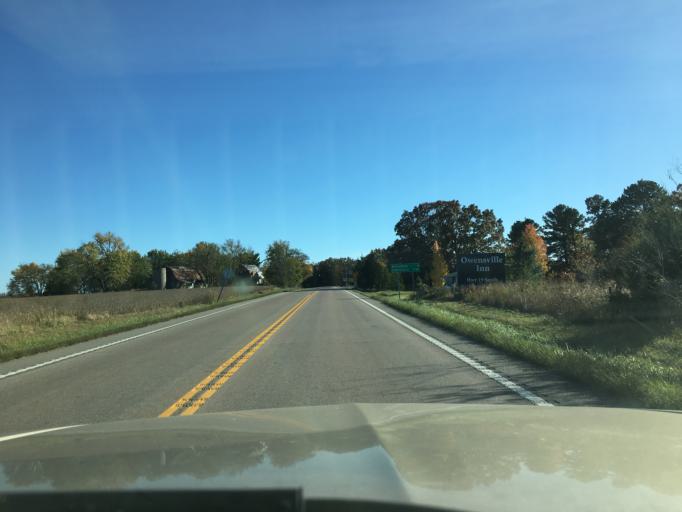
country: US
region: Missouri
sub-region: Gasconade County
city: Owensville
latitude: 38.4607
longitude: -91.4645
